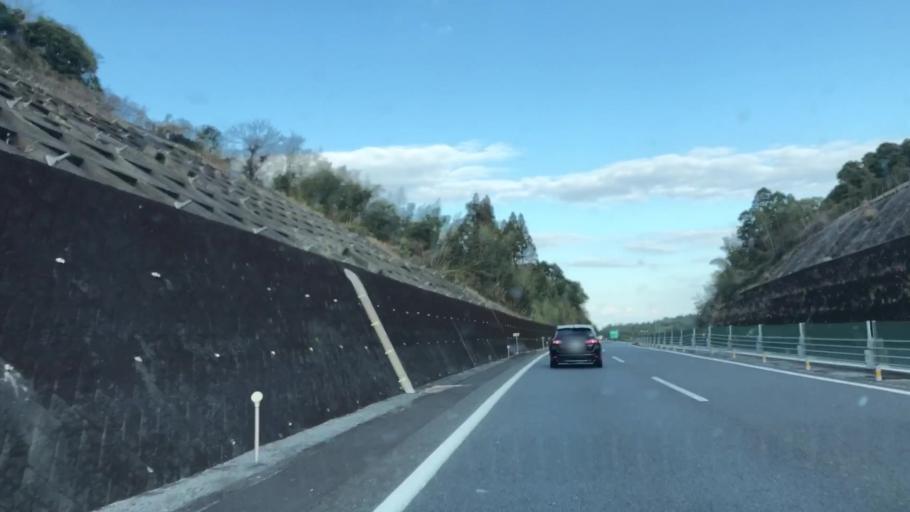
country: JP
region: Miyazaki
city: Miyazaki-shi
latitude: 31.8653
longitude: 131.3851
